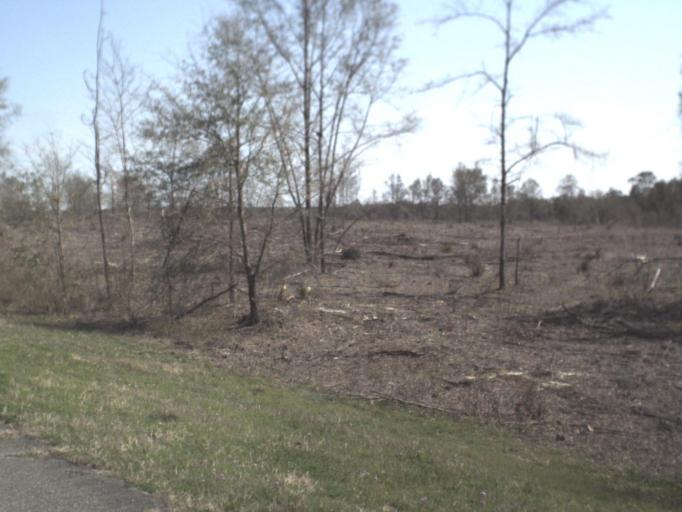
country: US
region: Florida
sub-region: Liberty County
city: Bristol
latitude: 30.5064
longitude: -84.8411
